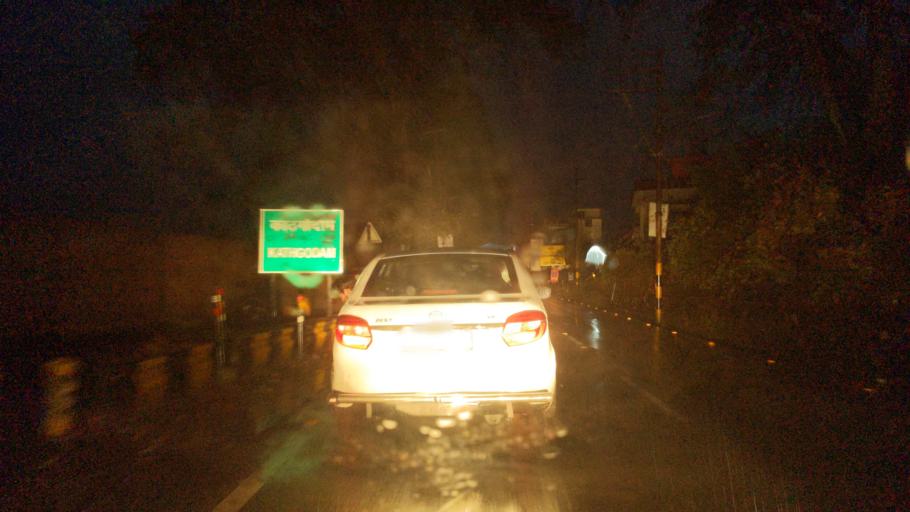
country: IN
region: Uttarakhand
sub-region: Naini Tal
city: Haldwani
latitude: 29.2762
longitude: 79.5455
